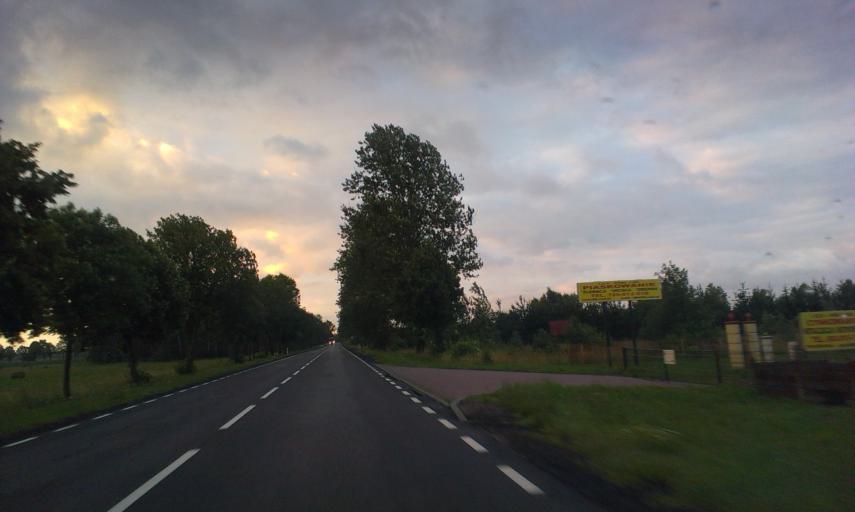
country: PL
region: West Pomeranian Voivodeship
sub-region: Powiat szczecinecki
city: Szczecinek
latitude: 53.6507
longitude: 16.7465
